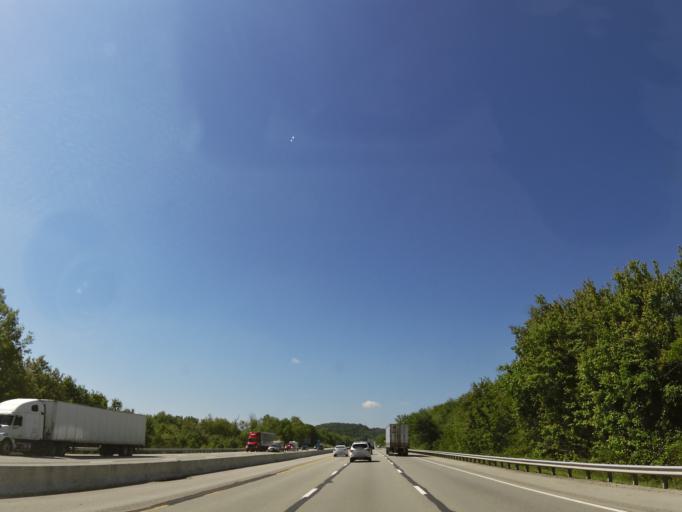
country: US
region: Kentucky
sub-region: Madison County
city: Berea
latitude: 37.5591
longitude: -84.3159
